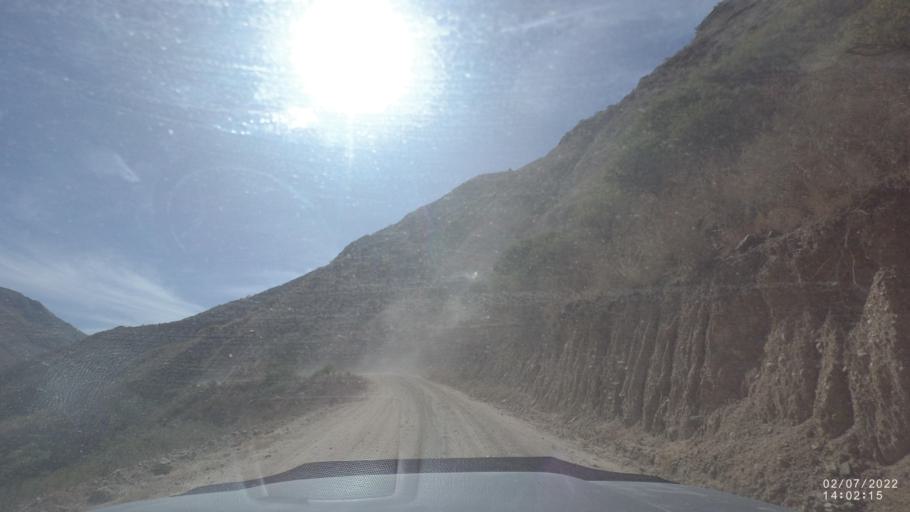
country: BO
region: Cochabamba
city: Irpa Irpa
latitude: -17.8244
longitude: -66.3865
